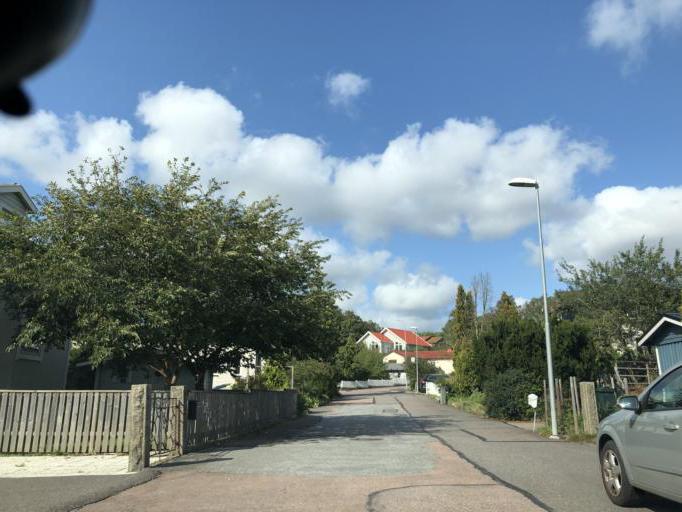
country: SE
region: Vaestra Goetaland
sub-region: Goteborg
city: Goeteborg
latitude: 57.7384
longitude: 11.9610
